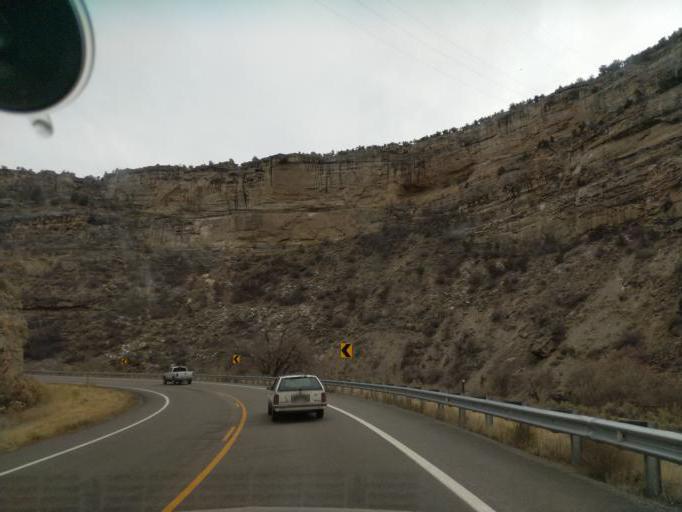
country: US
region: Colorado
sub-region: Mesa County
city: Palisade
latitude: 39.1920
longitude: -108.2365
